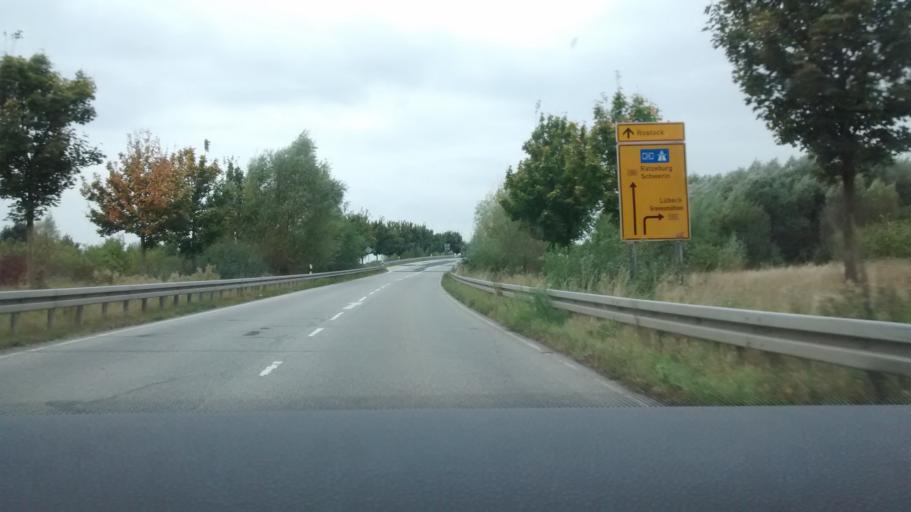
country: DE
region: Mecklenburg-Vorpommern
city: Wismar
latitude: 53.8878
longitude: 11.4231
